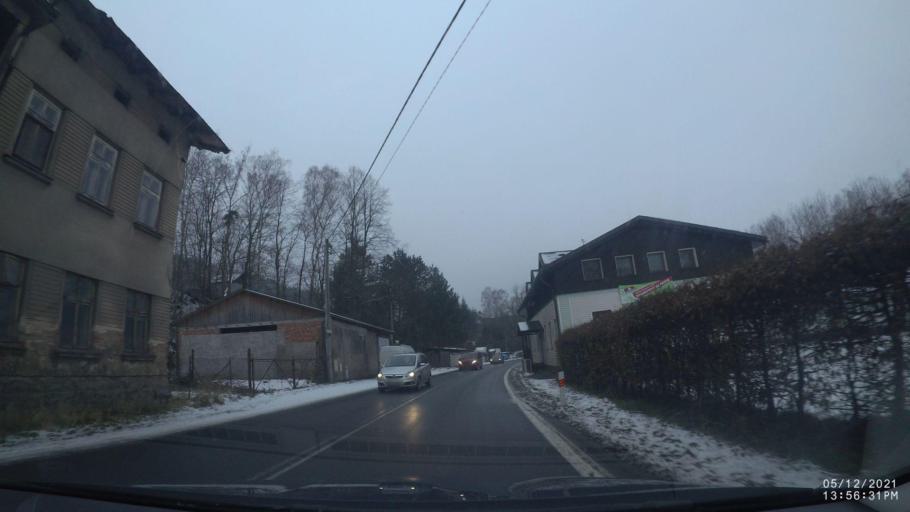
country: CZ
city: Hronov
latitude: 50.4922
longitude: 16.1914
